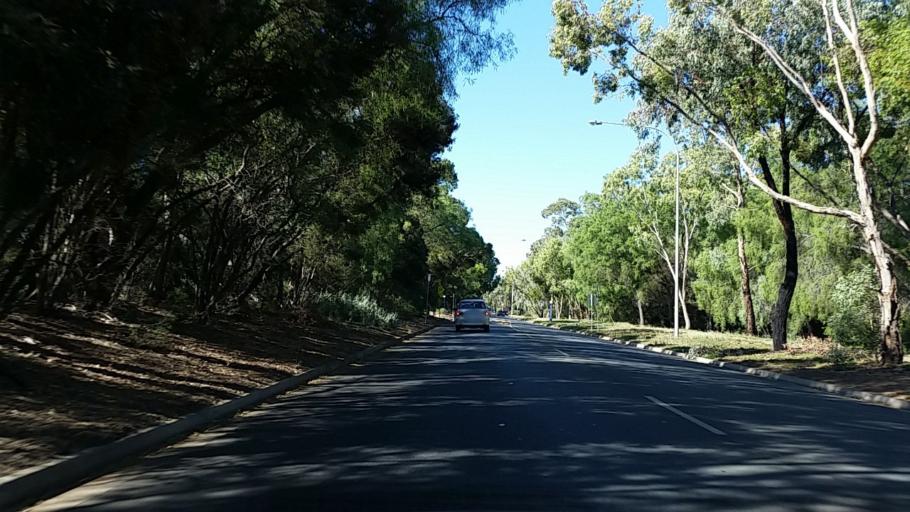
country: AU
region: South Australia
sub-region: Salisbury
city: Salisbury
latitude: -34.7794
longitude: 138.6105
